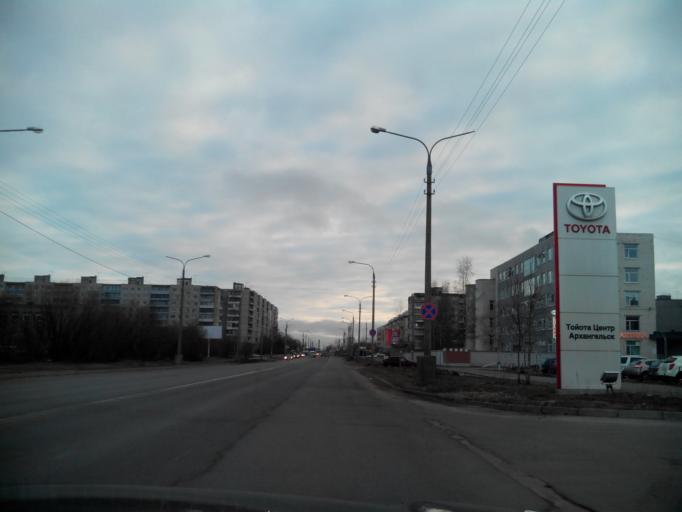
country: RU
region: Arkhangelskaya
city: Arkhangel'sk
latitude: 64.5166
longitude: 40.6743
